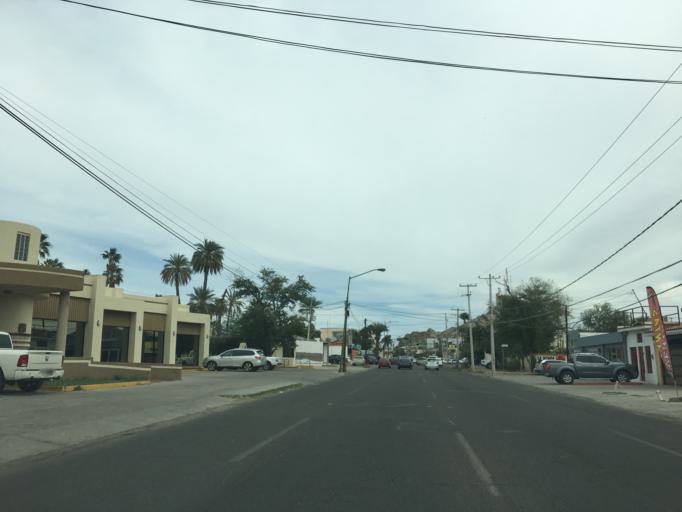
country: MX
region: Sonora
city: Hermosillo
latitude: 29.0739
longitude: -110.9669
